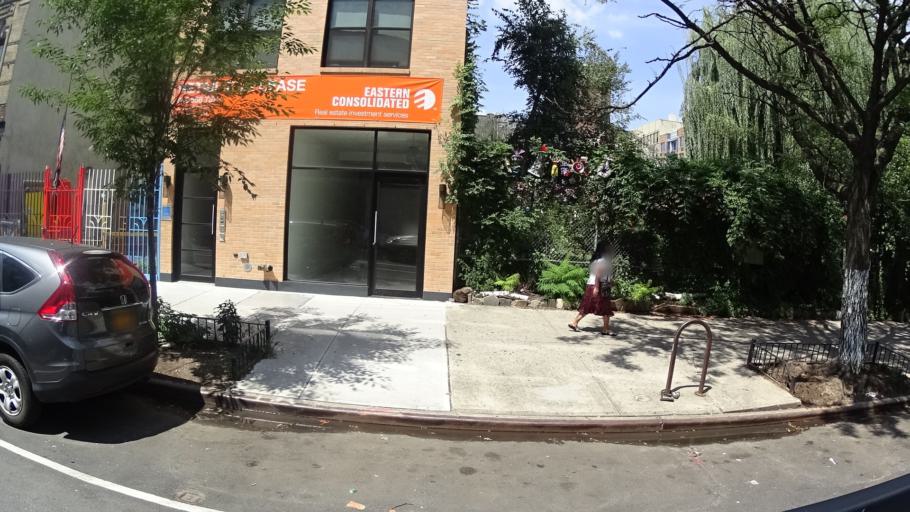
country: US
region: New York
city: New York City
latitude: 40.7251
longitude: -73.9782
